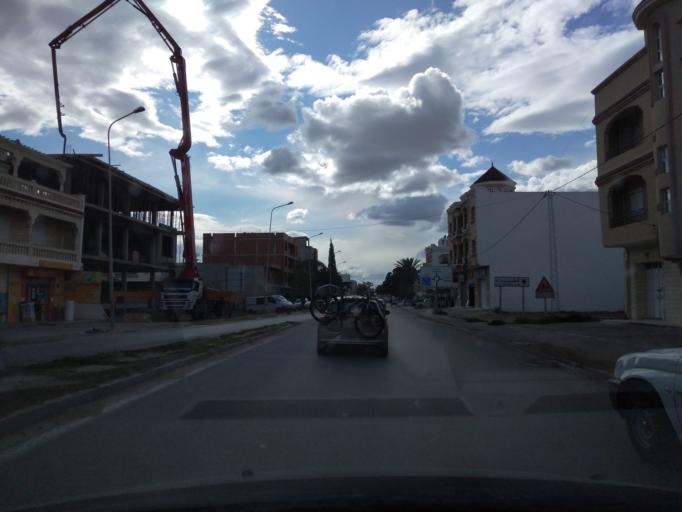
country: TN
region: Susah
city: Masakin
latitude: 35.7199
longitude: 10.5665
